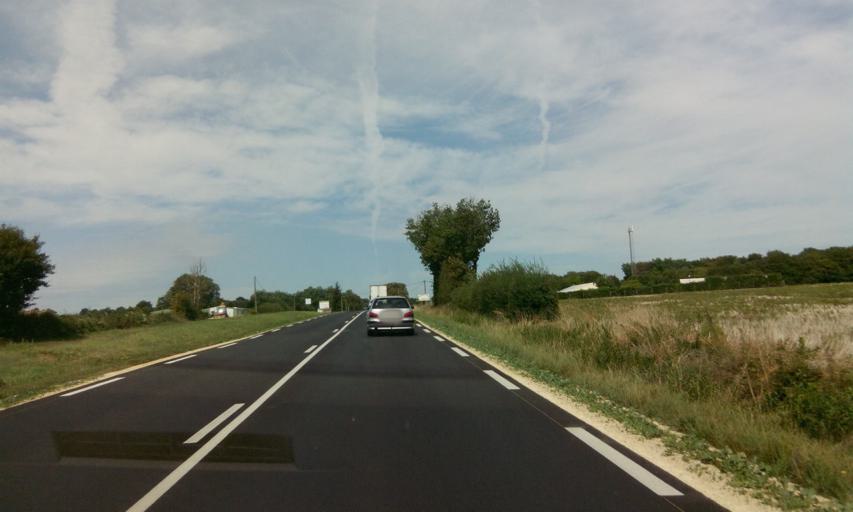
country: FR
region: Poitou-Charentes
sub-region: Departement des Deux-Sevres
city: Sauze-Vaussais
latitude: 46.1473
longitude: 0.0726
